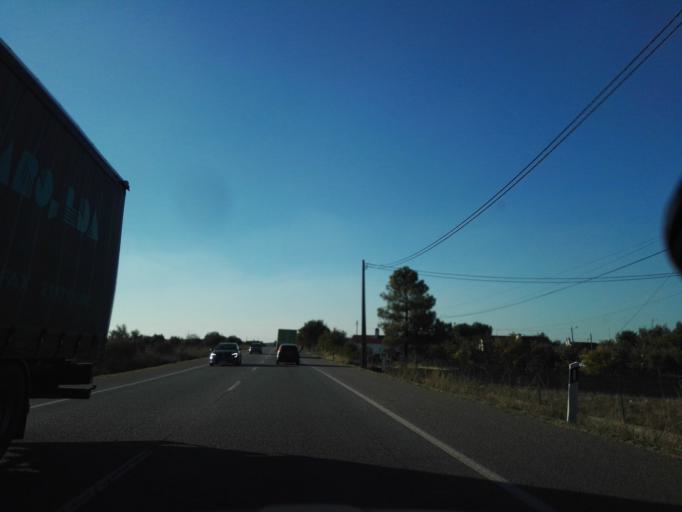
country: PT
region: Evora
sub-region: Borba
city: Borba
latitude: 38.8184
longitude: -7.4856
